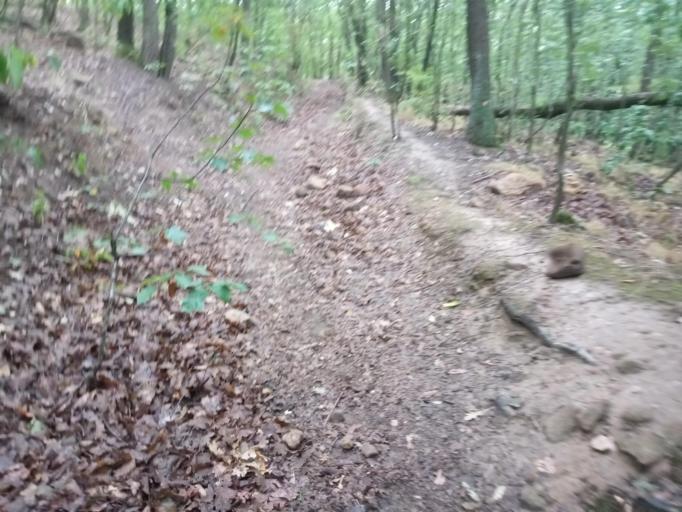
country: HU
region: Pest
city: Csobanka
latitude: 47.6387
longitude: 18.9755
